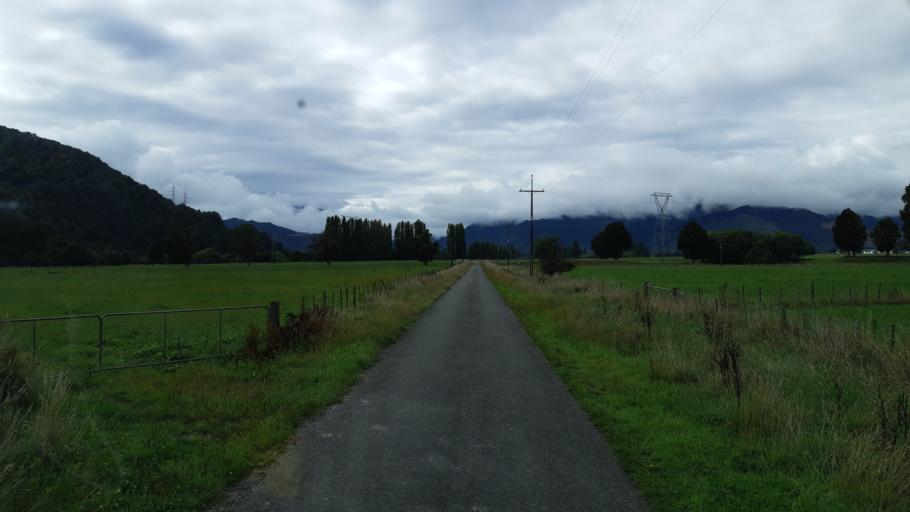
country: NZ
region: West Coast
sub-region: Buller District
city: Westport
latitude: -41.7757
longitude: 172.2888
